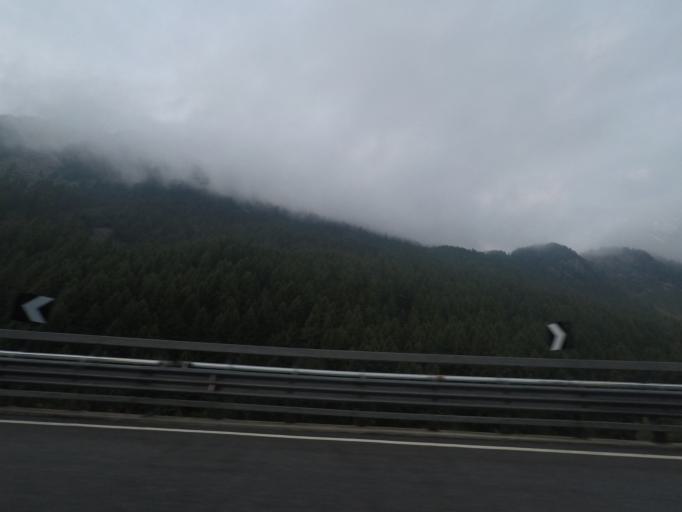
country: IT
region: Aosta Valley
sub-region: Valle d'Aosta
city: San Leonardo
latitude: 45.8198
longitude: 7.1444
